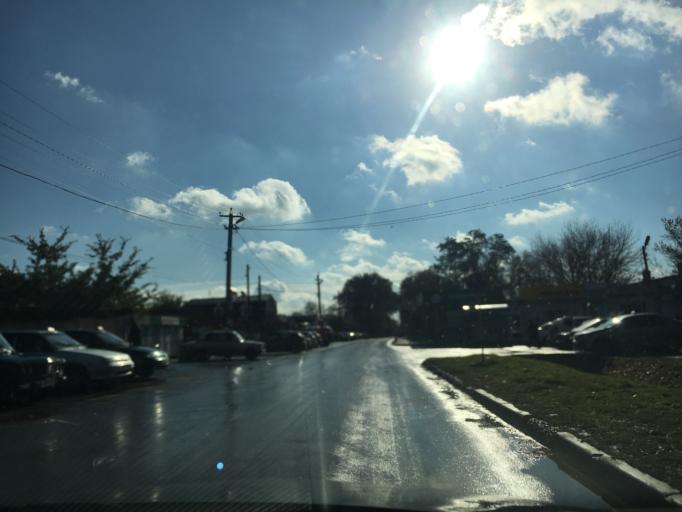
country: RU
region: Rostov
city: Matveyev Kurgan
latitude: 47.5647
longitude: 38.8608
